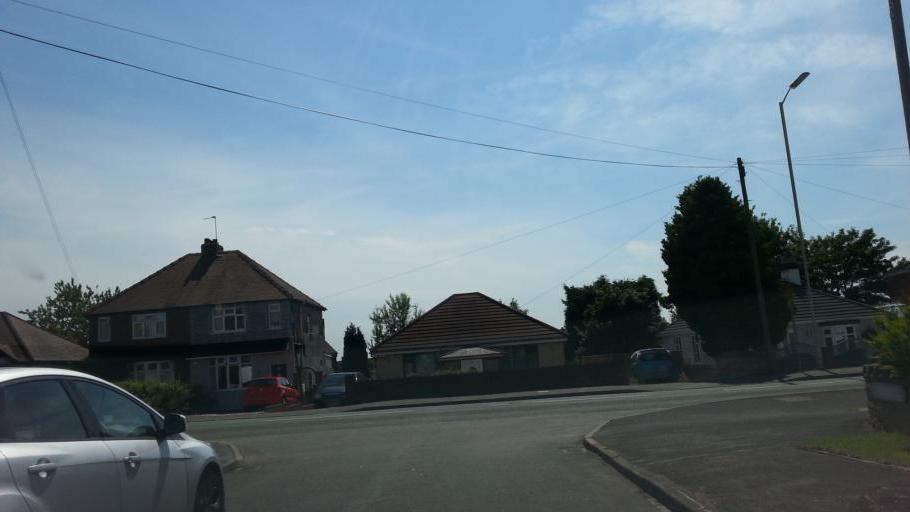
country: GB
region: England
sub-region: Staffordshire
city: Cannock
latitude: 52.7100
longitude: -2.0152
